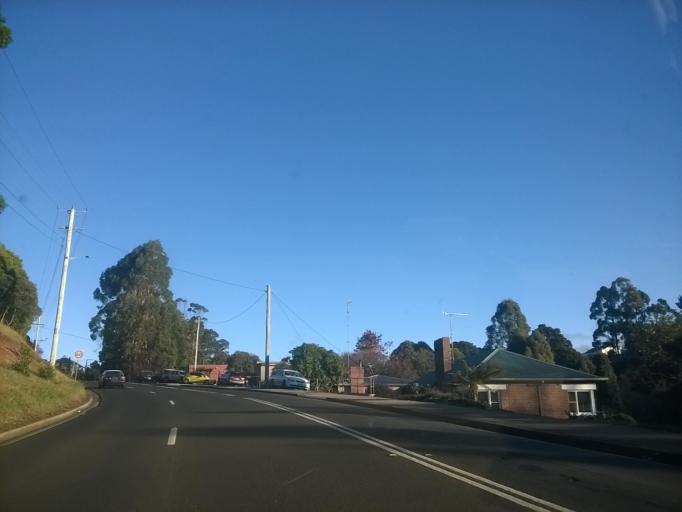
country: AU
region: Tasmania
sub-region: Burnie
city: Burnie
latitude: -41.0630
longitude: 145.9022
